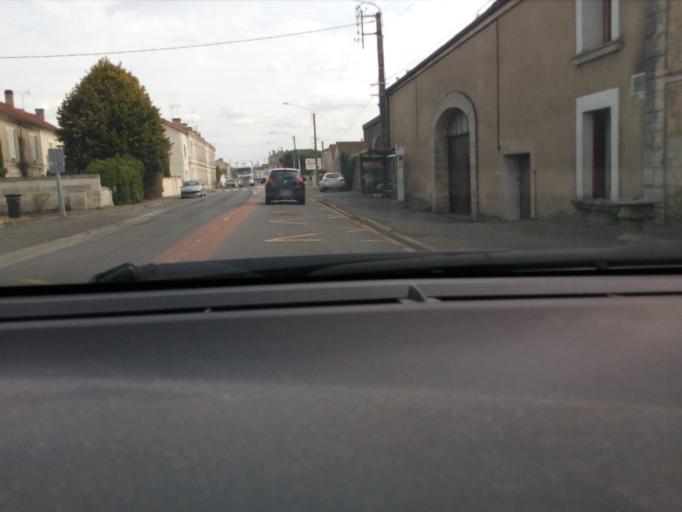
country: FR
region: Poitou-Charentes
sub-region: Departement de la Charente
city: Saint-Yrieix-sur-Charente
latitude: 45.6680
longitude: 0.1202
